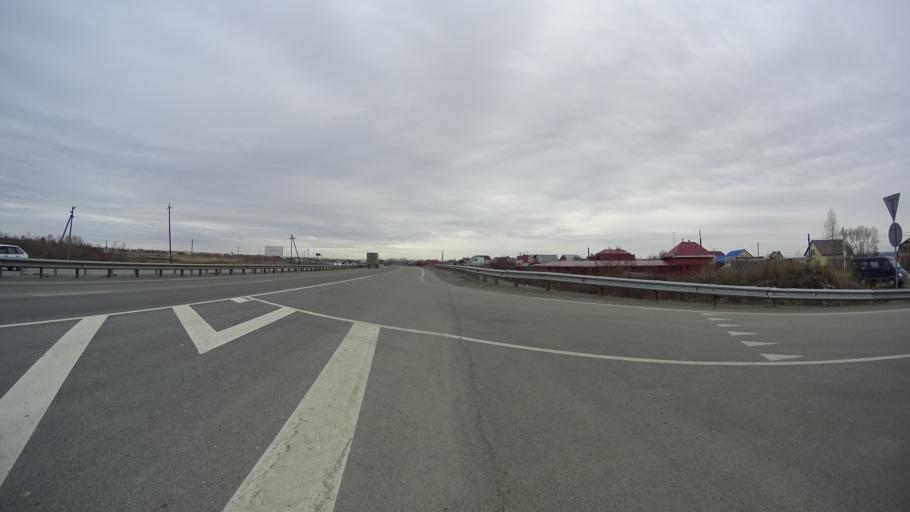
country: RU
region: Chelyabinsk
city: Novosineglazovskiy
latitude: 55.0126
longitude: 61.4506
